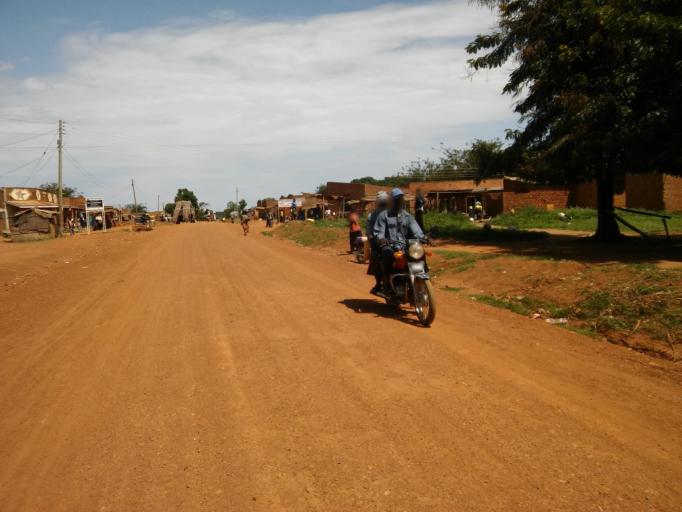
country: UG
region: Eastern Region
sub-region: Kumi District
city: Kumi
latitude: 1.4719
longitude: 33.8674
